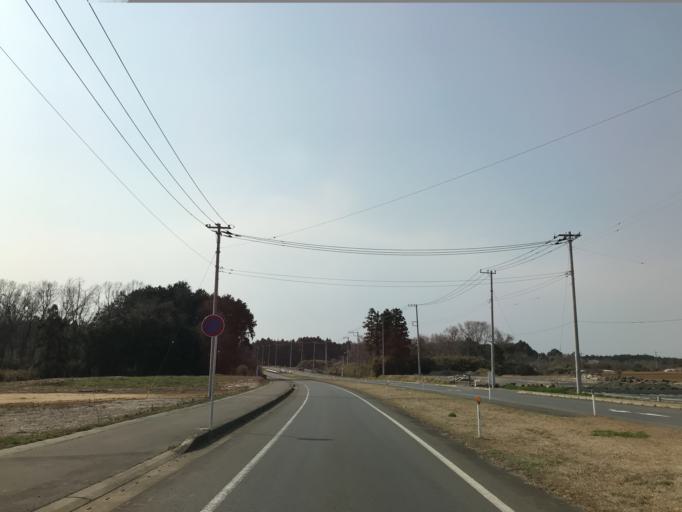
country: JP
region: Ibaraki
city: Okunoya
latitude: 36.1866
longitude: 140.3896
